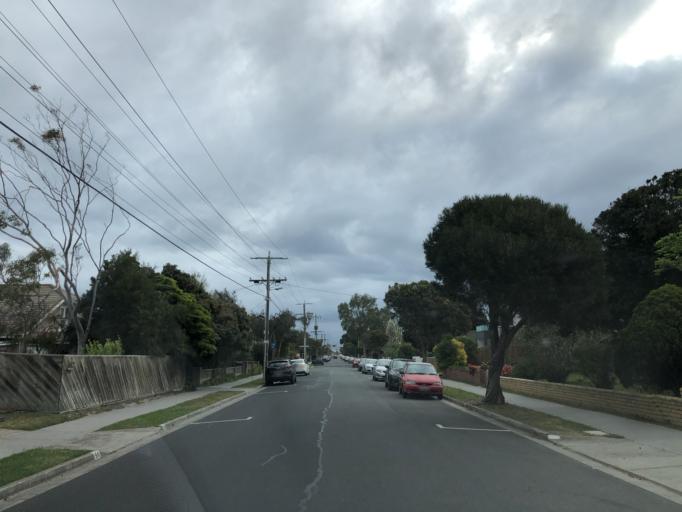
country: AU
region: Victoria
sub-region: Kingston
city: Bonbeach
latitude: -38.0617
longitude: 145.1257
